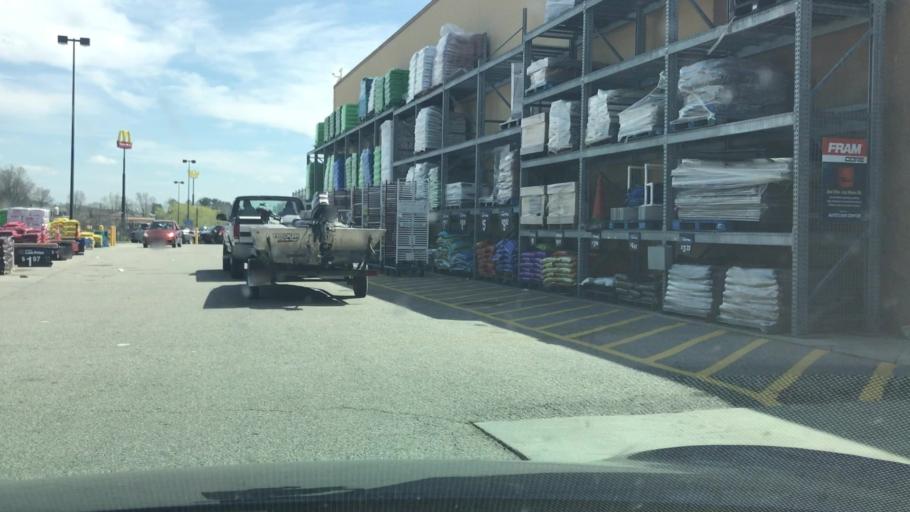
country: US
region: Virginia
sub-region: Pulaski County
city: Dublin
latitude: 37.0845
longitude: -80.6937
